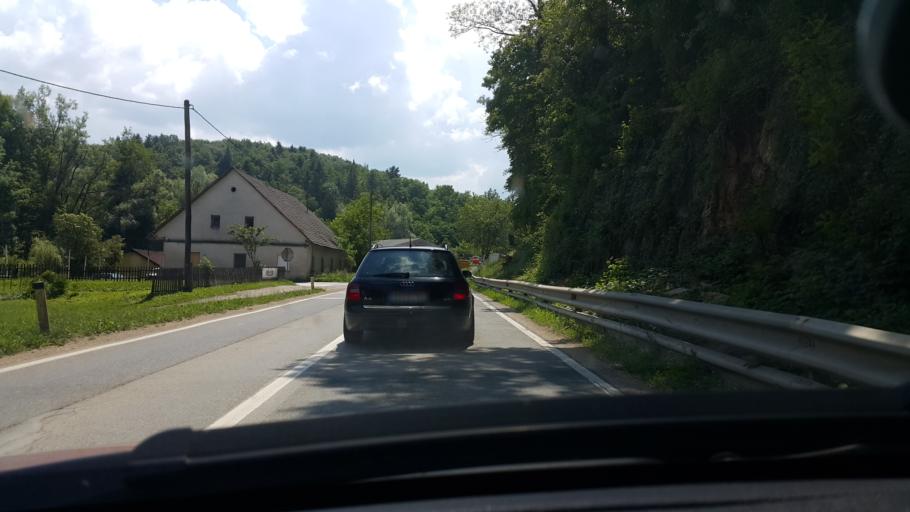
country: SI
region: Novo Mesto
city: Novo Mesto
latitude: 45.7792
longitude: 15.1787
